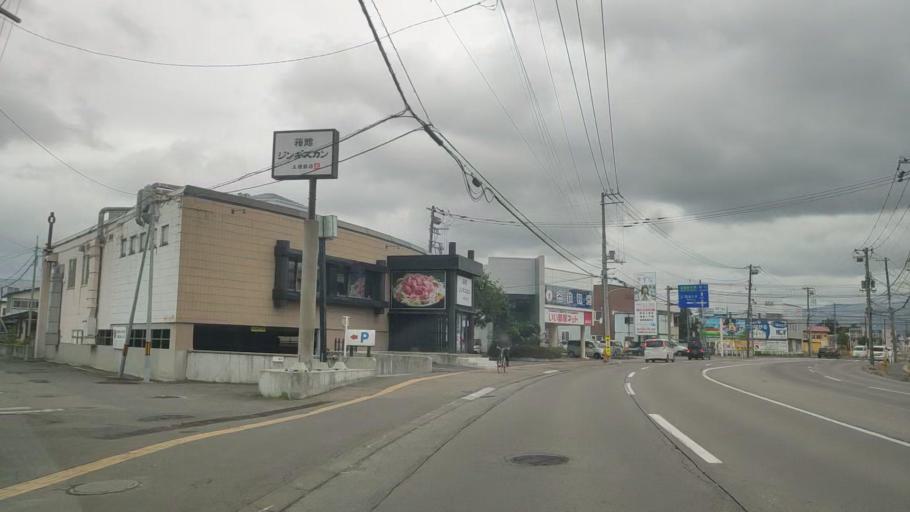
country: JP
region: Hokkaido
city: Hakodate
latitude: 41.7991
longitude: 140.7502
